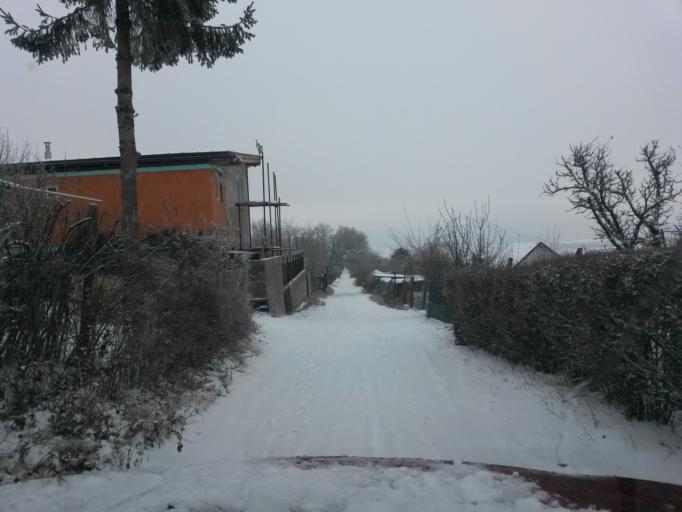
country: SK
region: Kosicky
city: Kosice
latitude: 48.7163
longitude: 21.3143
